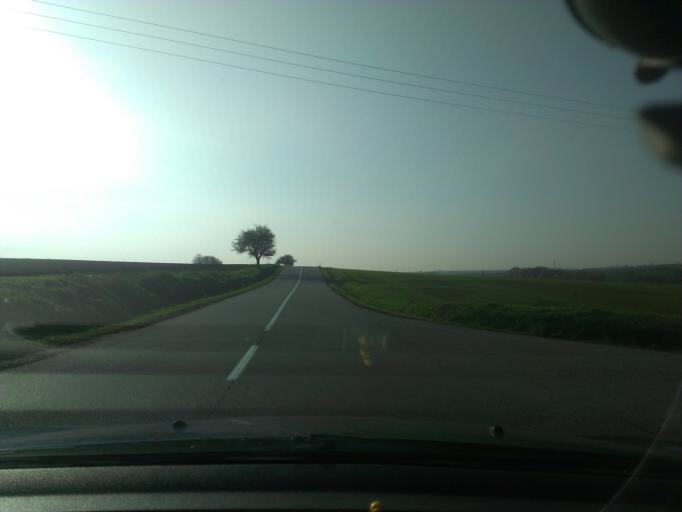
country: SK
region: Nitriansky
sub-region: Okres Nitra
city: Nitra
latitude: 48.4495
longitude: 17.9856
